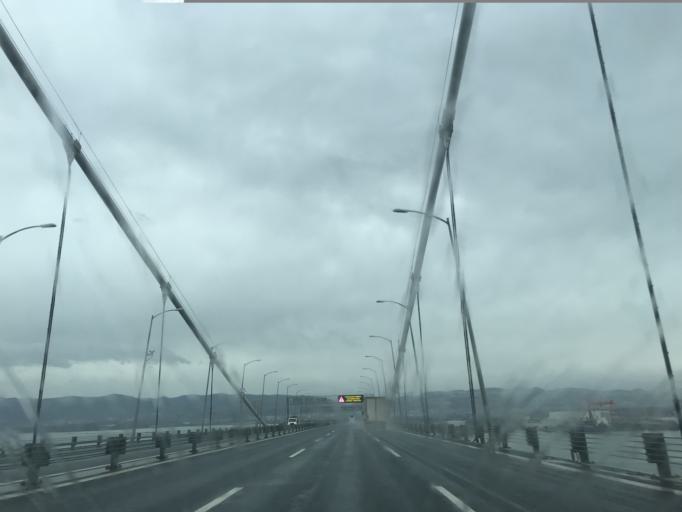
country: TR
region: Yalova
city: Altinova
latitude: 40.7451
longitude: 29.5141
